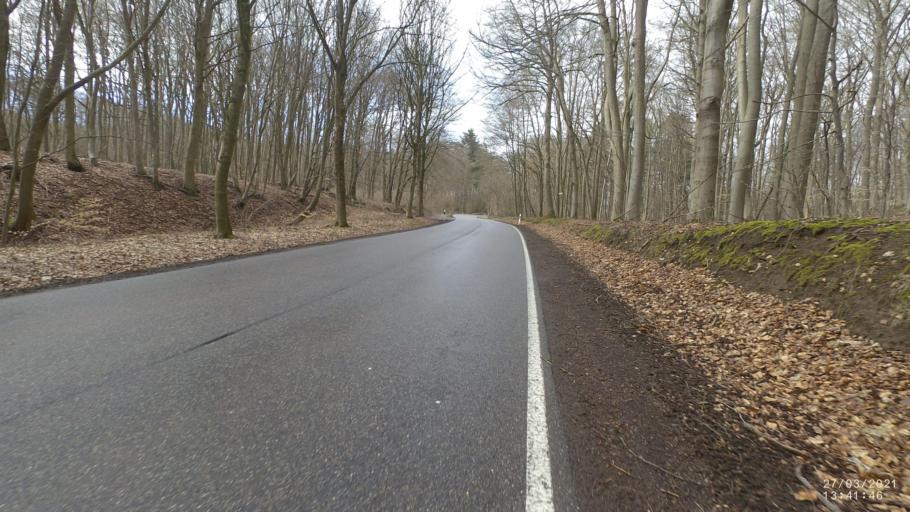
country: DE
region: Rheinland-Pfalz
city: Wassenach
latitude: 50.4237
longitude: 7.2947
